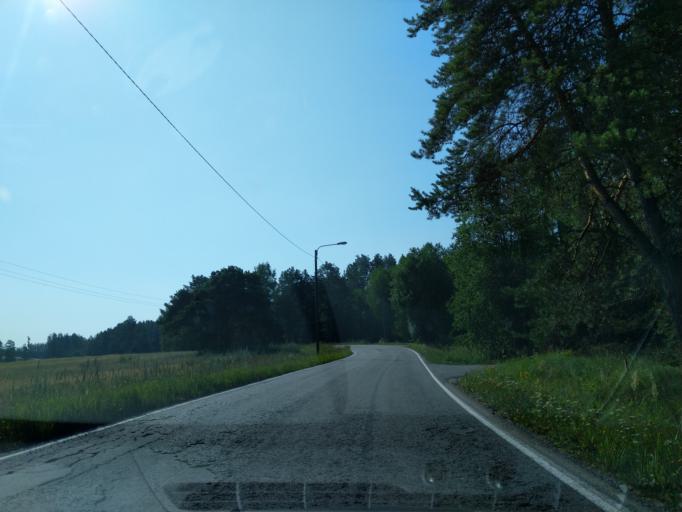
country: FI
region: Satakunta
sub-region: Pori
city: Noormarkku
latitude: 61.5873
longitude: 21.8952
